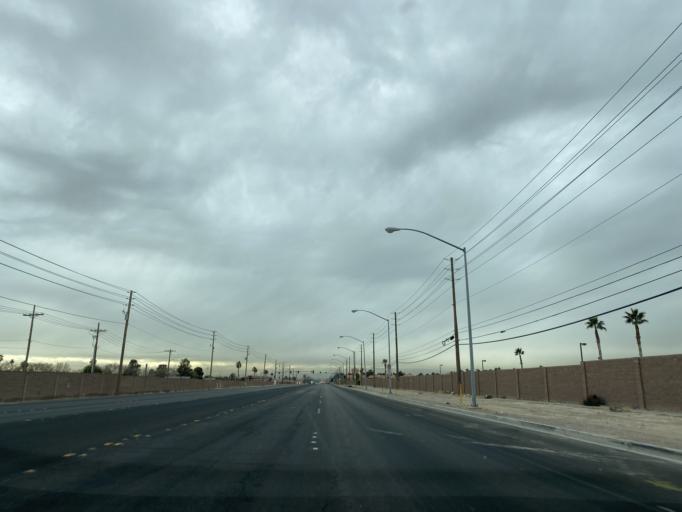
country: US
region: Nevada
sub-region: Clark County
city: Nellis Air Force Base
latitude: 36.2449
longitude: -115.0470
